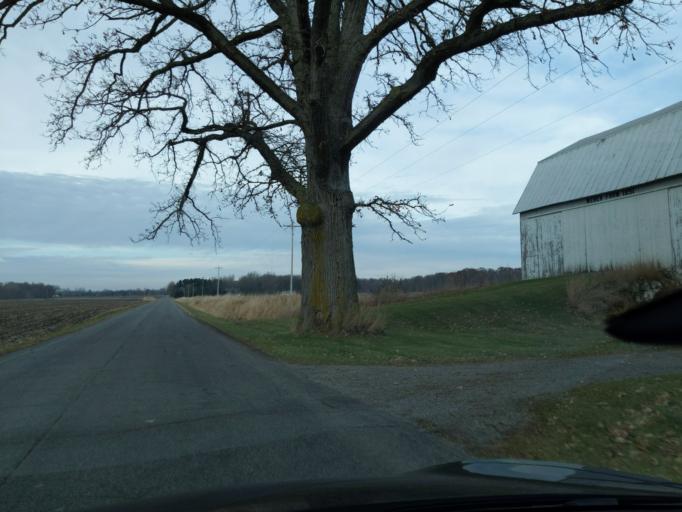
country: US
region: Michigan
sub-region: Ingham County
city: Okemos
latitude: 42.6603
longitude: -84.3835
